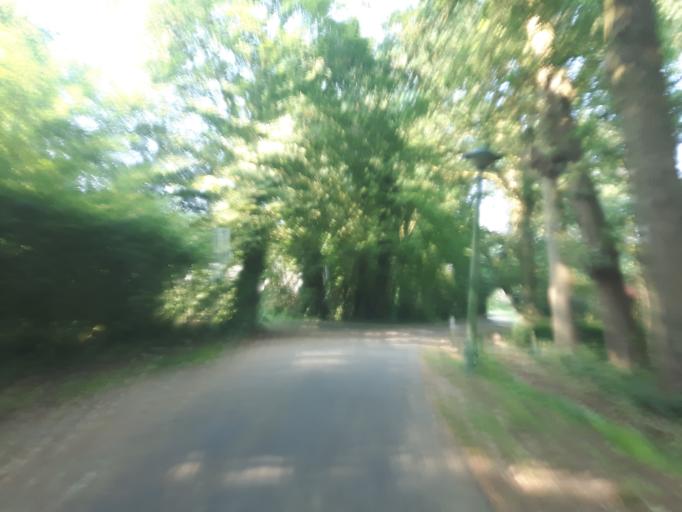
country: NL
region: Overijssel
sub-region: Gemeente Enschede
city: Enschede
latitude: 52.2045
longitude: 6.8332
